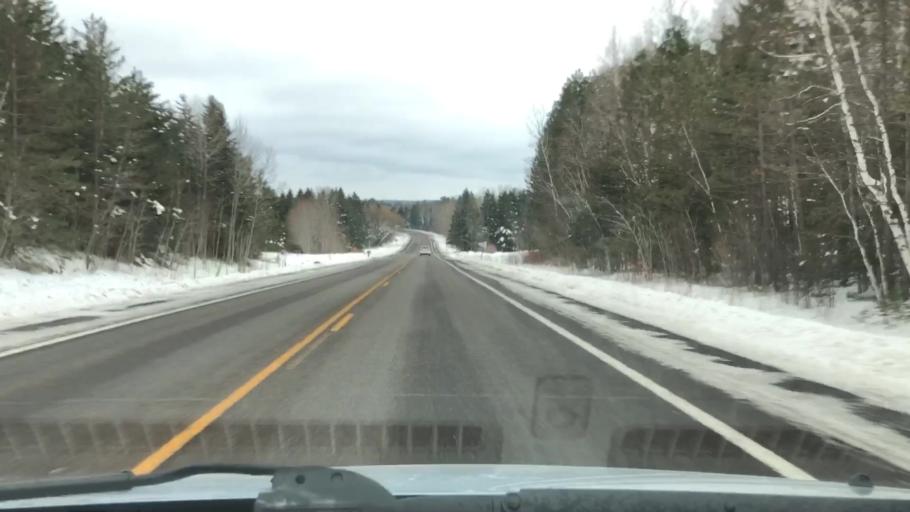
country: US
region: Minnesota
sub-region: Carlton County
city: Esko
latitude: 46.6763
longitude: -92.3777
